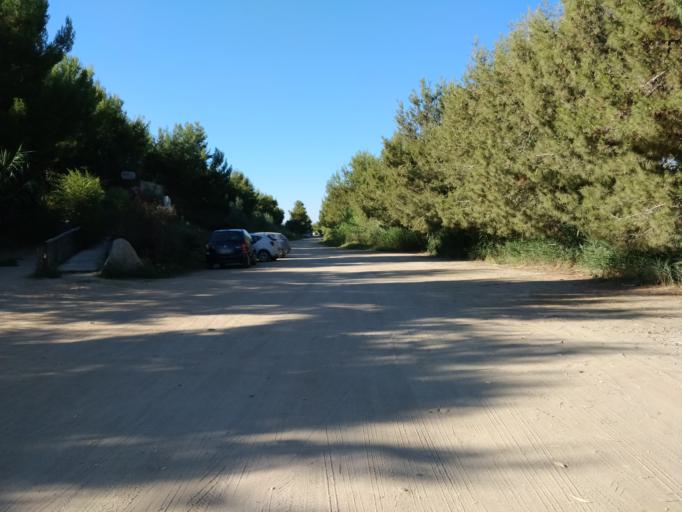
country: IT
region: Sardinia
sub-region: Provincia di Ogliastra
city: Lotzorai
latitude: 39.9592
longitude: 9.6833
